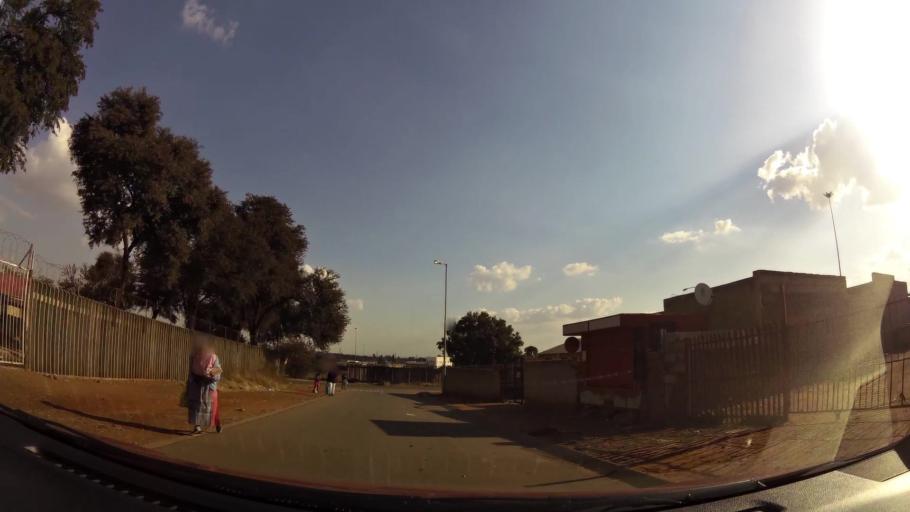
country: ZA
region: Gauteng
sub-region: City of Johannesburg Metropolitan Municipality
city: Soweto
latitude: -26.2329
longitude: 27.8671
